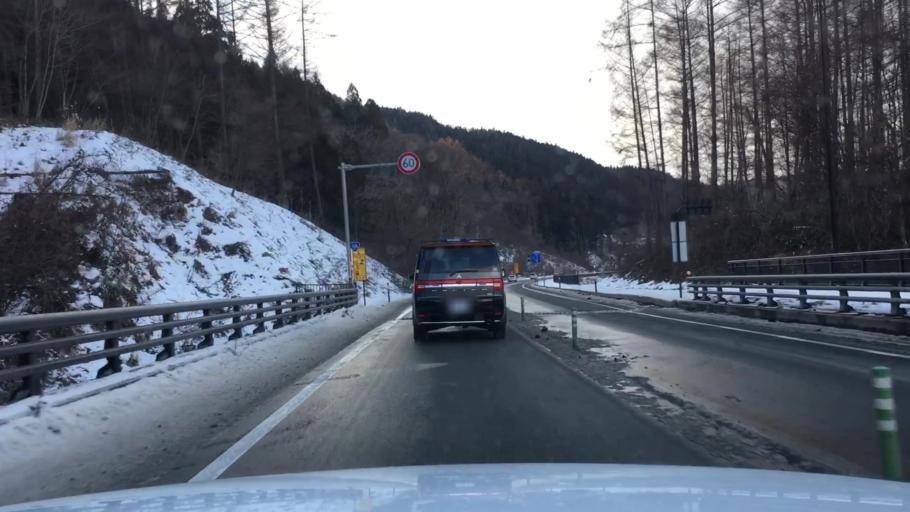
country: JP
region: Iwate
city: Morioka-shi
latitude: 39.6676
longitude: 141.2380
